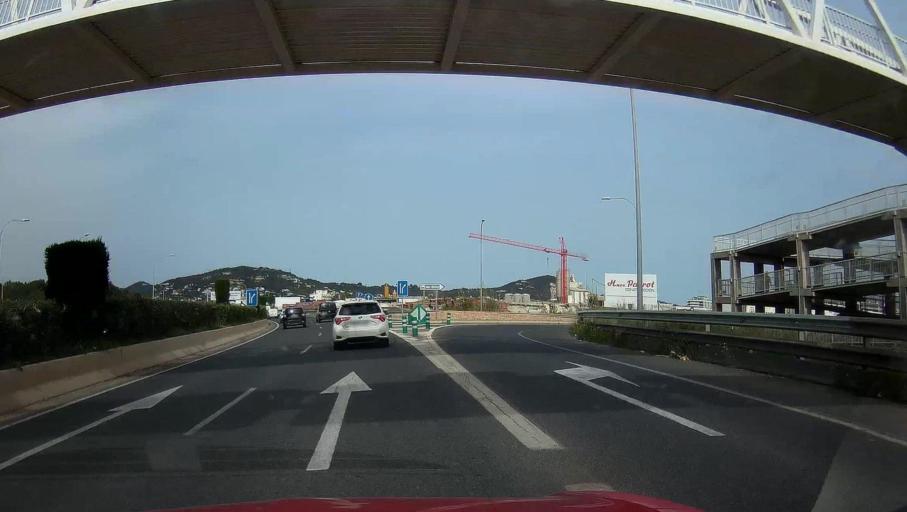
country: ES
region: Balearic Islands
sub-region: Illes Balears
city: Ibiza
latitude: 38.9212
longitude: 1.4353
